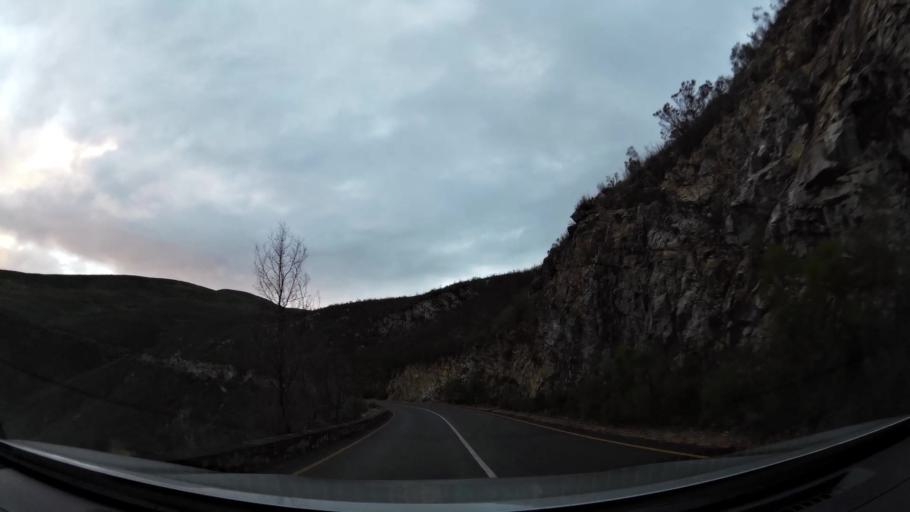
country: ZA
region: Western Cape
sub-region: Overberg District Municipality
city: Swellendam
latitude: -33.9823
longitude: 20.7090
